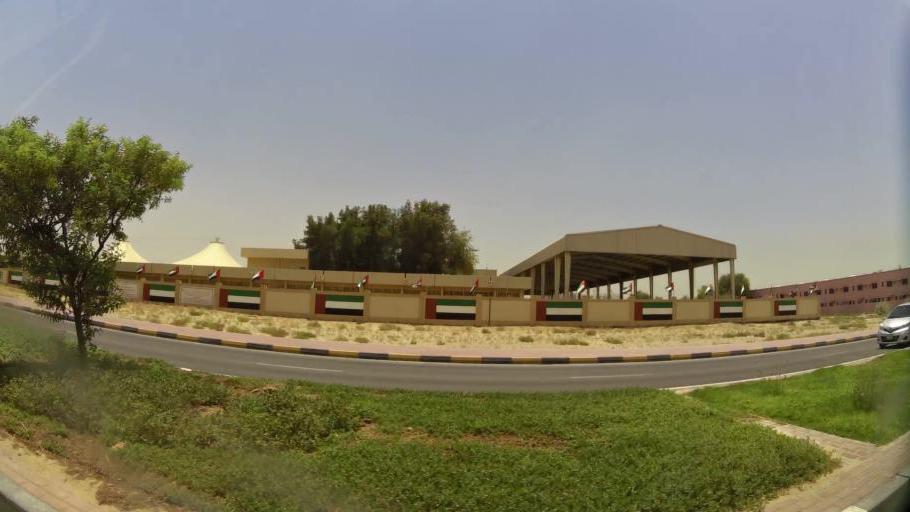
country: AE
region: Ajman
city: Ajman
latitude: 25.4056
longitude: 55.4932
